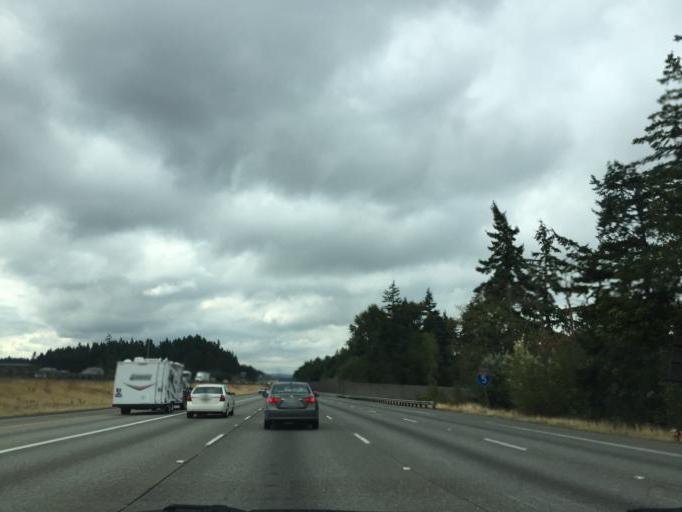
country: US
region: Washington
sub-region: King County
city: Federal Way
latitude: 47.3053
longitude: -122.3016
